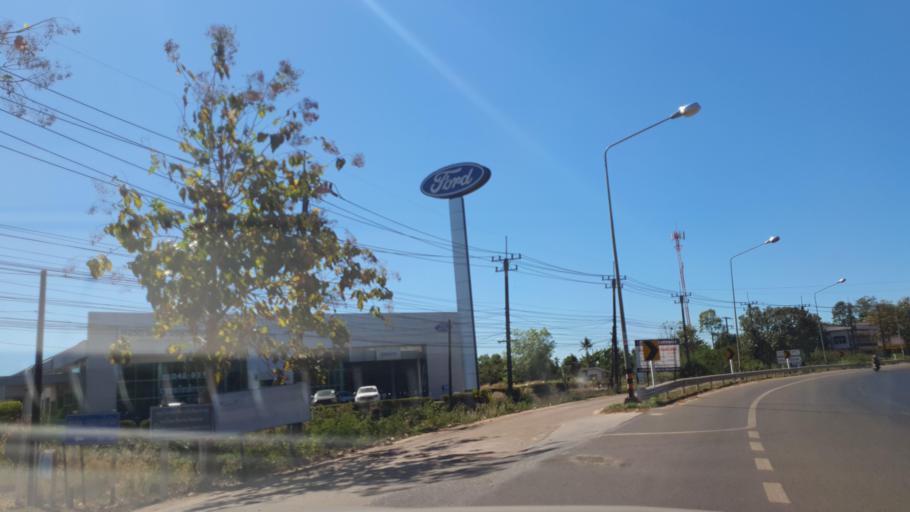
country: TH
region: Nakhon Phanom
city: Nakhon Phanom
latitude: 17.3825
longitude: 104.7568
